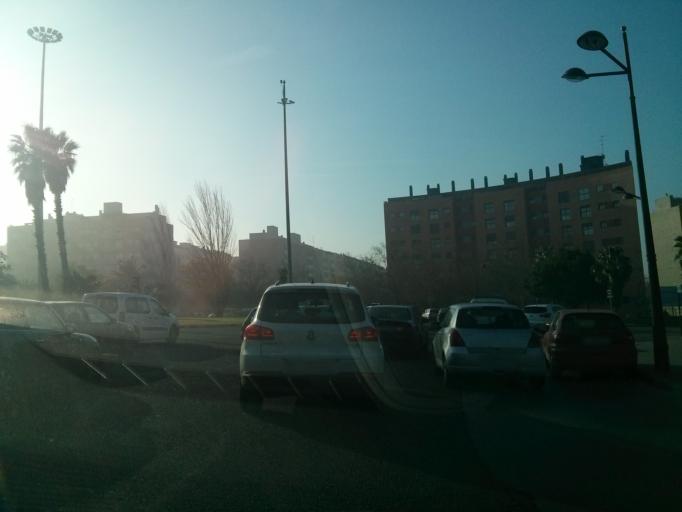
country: ES
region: Valencia
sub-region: Provincia de Valencia
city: Tavernes Blanques
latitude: 39.4979
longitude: -0.3868
